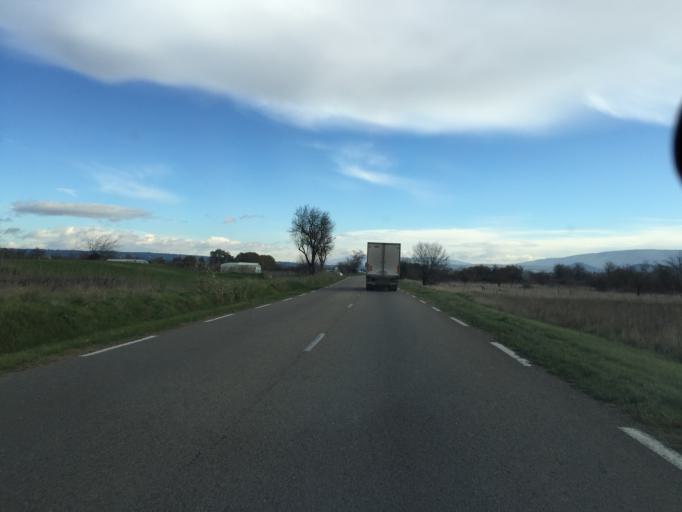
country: FR
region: Provence-Alpes-Cote d'Azur
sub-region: Departement du Vaucluse
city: Maubec
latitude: 43.8673
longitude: 5.1519
